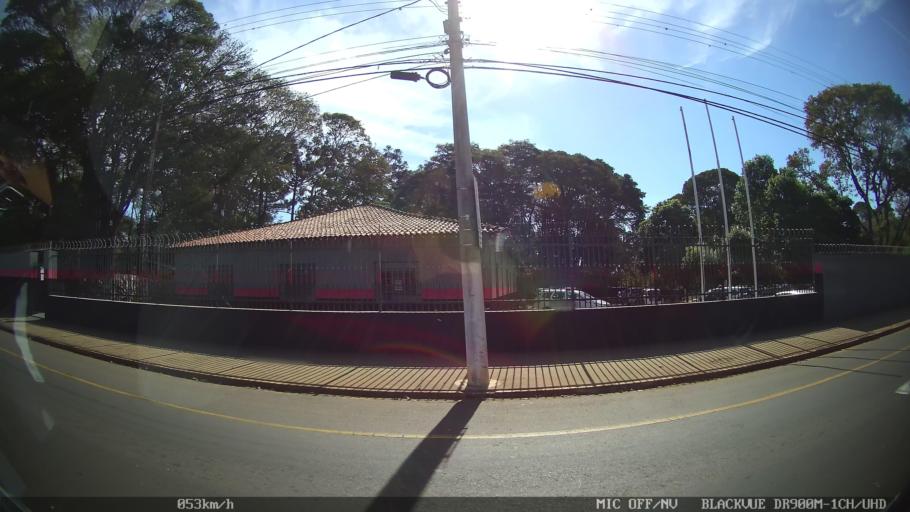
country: BR
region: Sao Paulo
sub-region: Franca
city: Franca
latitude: -20.5138
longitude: -47.4055
